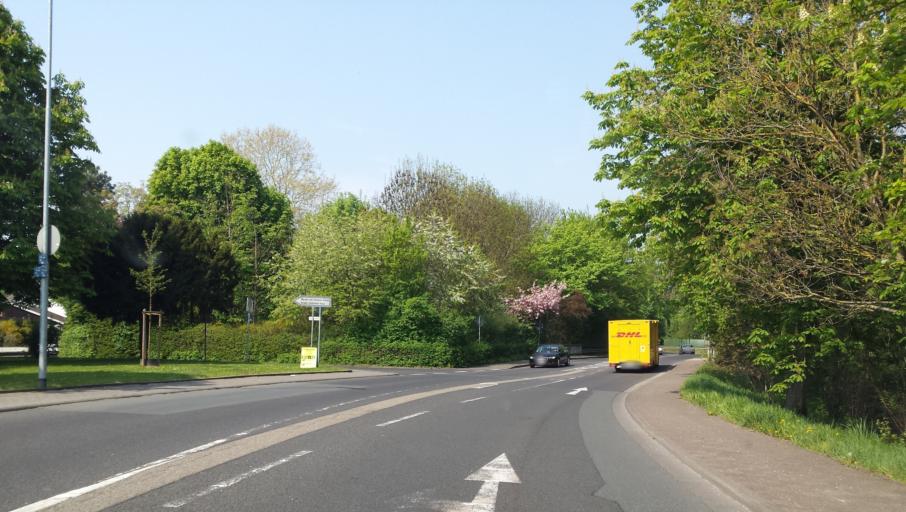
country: DE
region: Hesse
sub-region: Regierungsbezirk Darmstadt
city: Maintal
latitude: 50.1412
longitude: 8.8330
